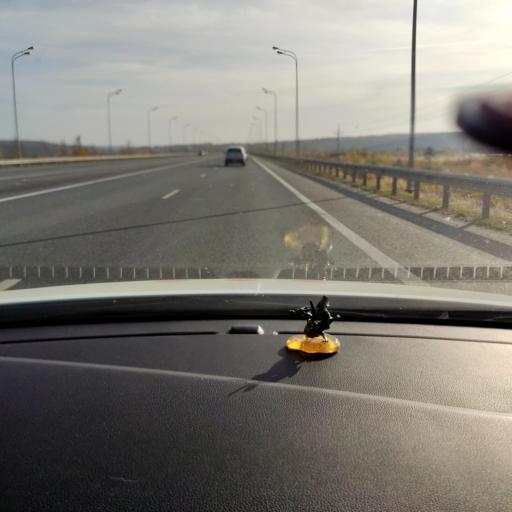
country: RU
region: Tatarstan
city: Osinovo
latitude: 55.8059
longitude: 48.8415
